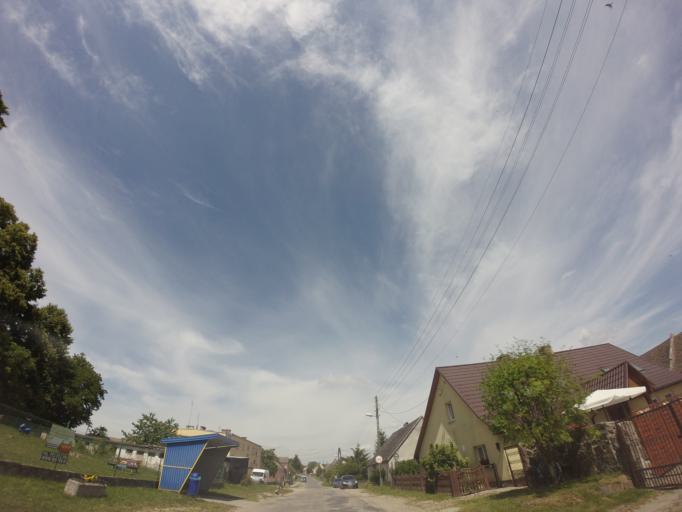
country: PL
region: West Pomeranian Voivodeship
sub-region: Powiat choszczenski
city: Recz
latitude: 53.3452
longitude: 15.5433
